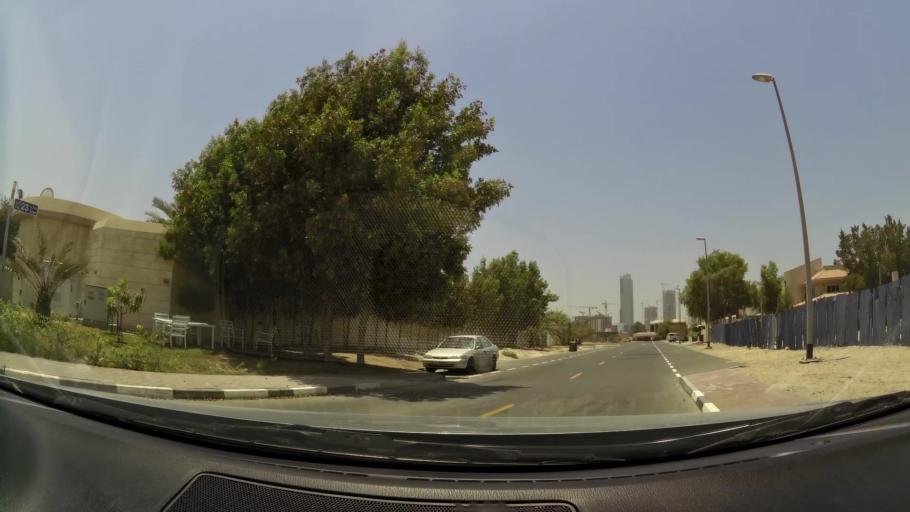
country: AE
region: Dubai
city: Dubai
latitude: 25.1008
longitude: 55.1893
